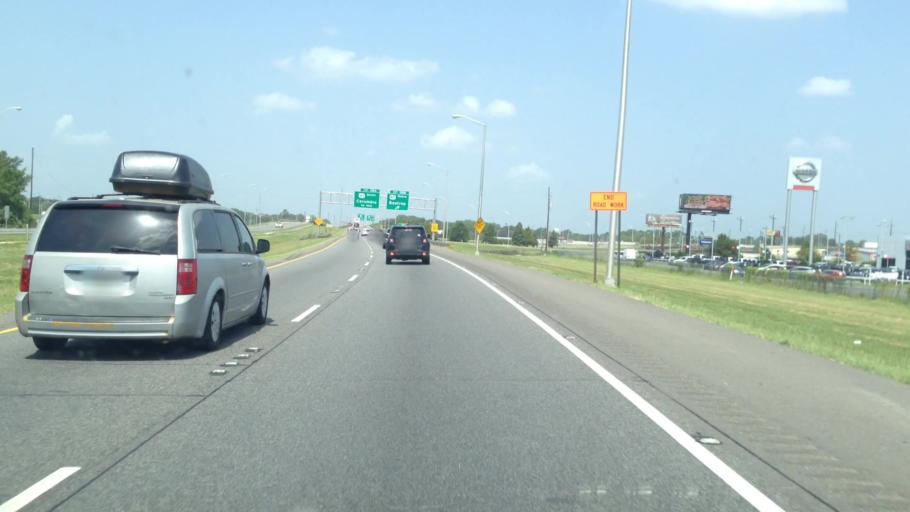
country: US
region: Louisiana
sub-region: Ouachita Parish
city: Monroe
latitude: 32.4990
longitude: -92.0773
